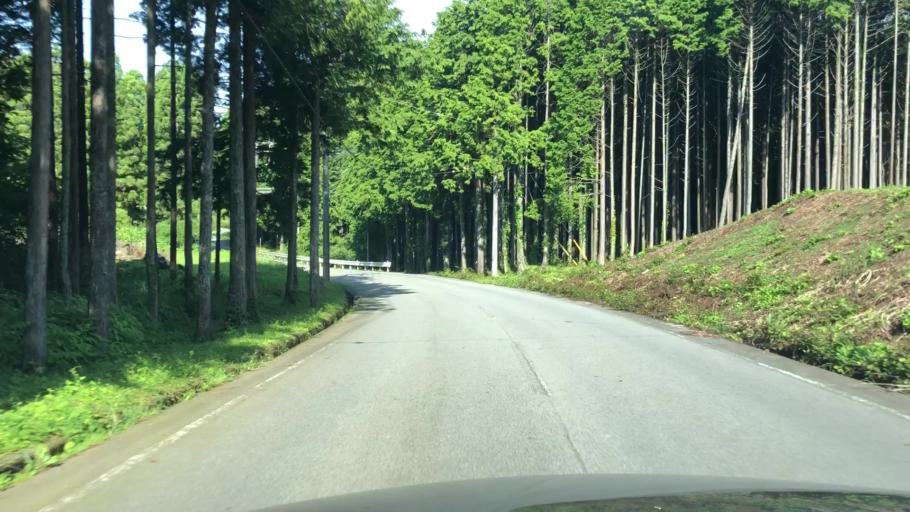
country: JP
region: Shizuoka
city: Gotemba
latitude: 35.3224
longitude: 138.8927
